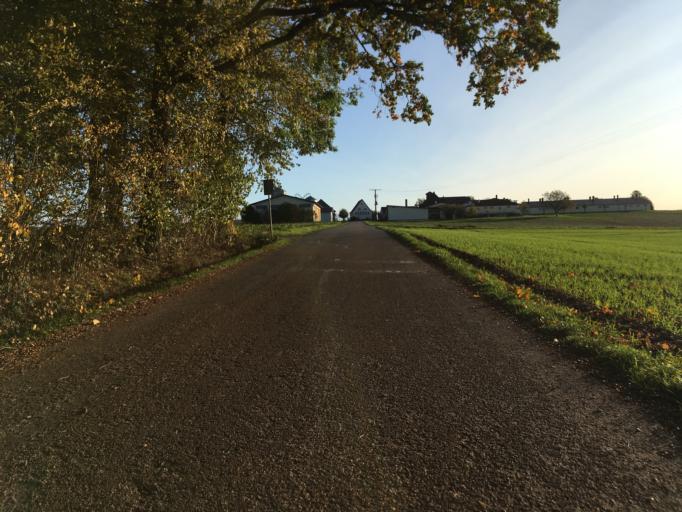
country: DE
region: Baden-Wuerttemberg
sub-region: Regierungsbezirk Stuttgart
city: Neuenstein
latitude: 49.2312
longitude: 9.6114
